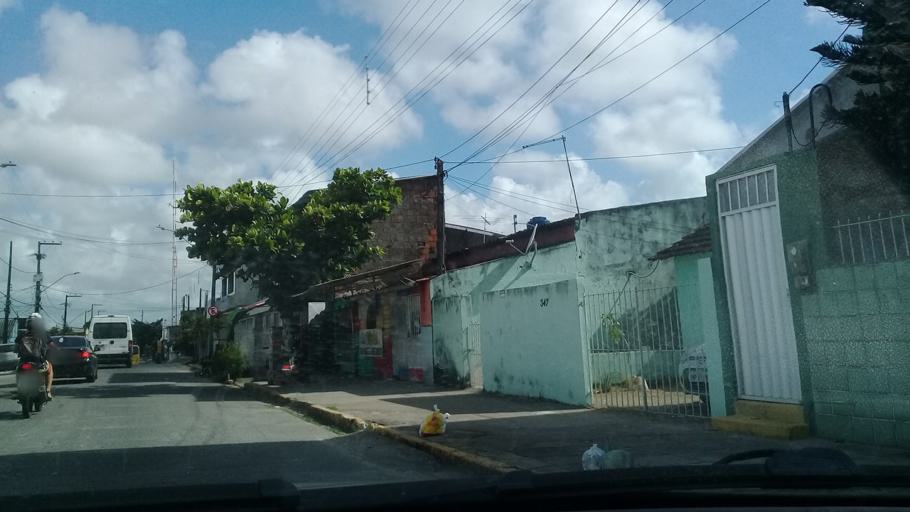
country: BR
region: Pernambuco
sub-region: Jaboatao Dos Guararapes
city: Jaboatao dos Guararapes
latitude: -8.1137
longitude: -34.9497
